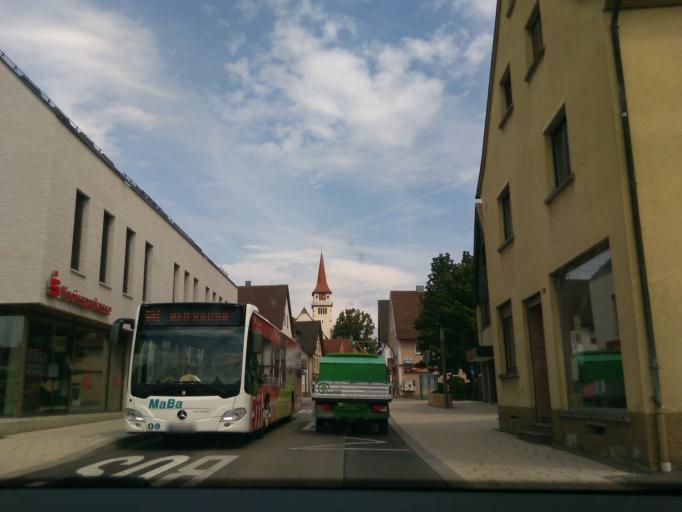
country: DE
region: Baden-Wuerttemberg
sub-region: Regierungsbezirk Stuttgart
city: Ilsfeld
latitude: 49.0551
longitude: 9.2425
